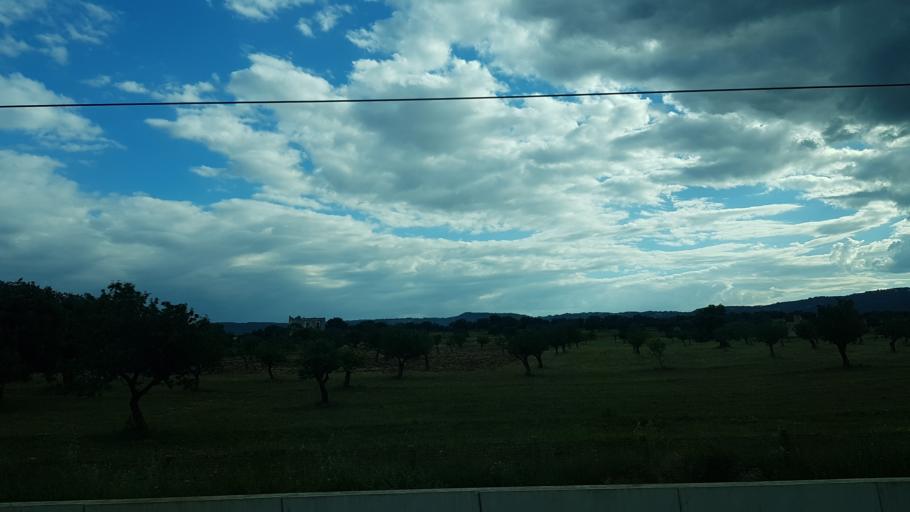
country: IT
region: Apulia
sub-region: Provincia di Brindisi
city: Pezze di Greco
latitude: 40.8440
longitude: 17.3976
